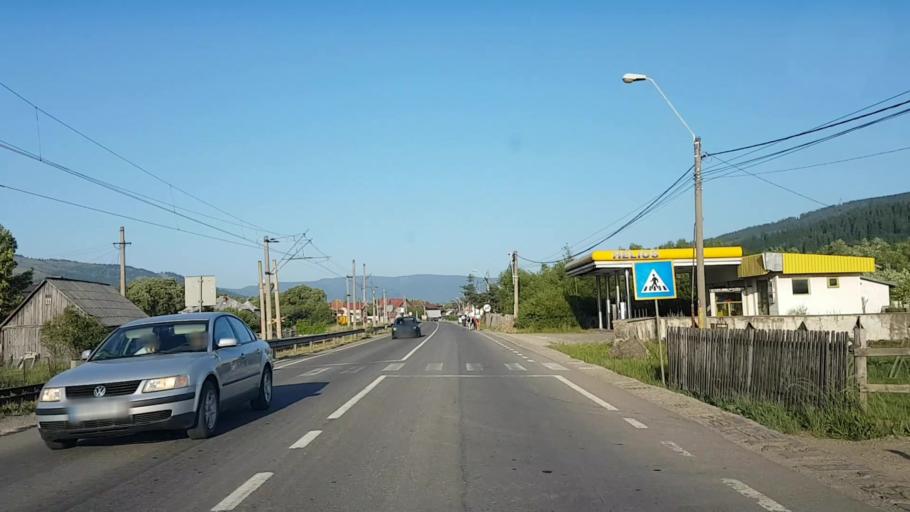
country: RO
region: Suceava
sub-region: Municipiul Vatra Dornei
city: Vatra Dornei
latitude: 47.3475
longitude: 25.3192
